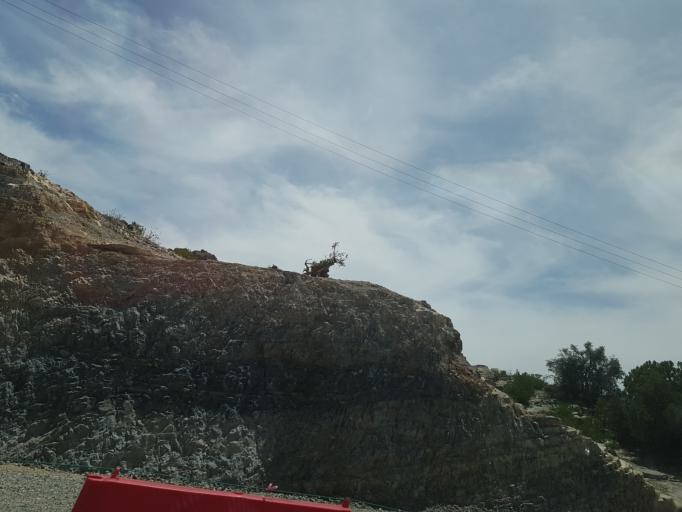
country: OM
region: Muhafazat ad Dakhiliyah
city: Nizwa
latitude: 23.1136
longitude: 57.6489
